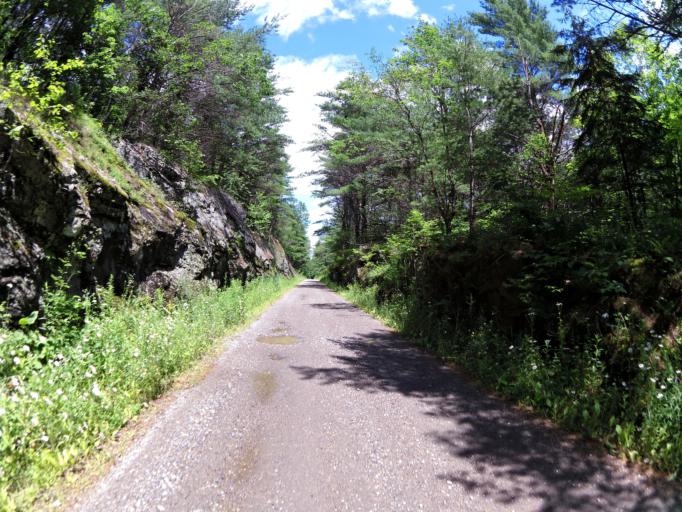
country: CA
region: Ontario
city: Renfrew
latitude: 45.0969
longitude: -76.7116
